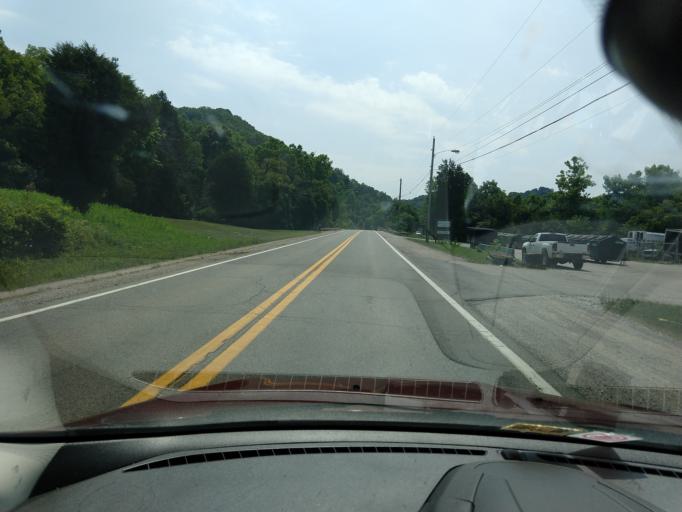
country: US
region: West Virginia
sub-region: Jackson County
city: Ravenswood
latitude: 38.8698
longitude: -81.8219
